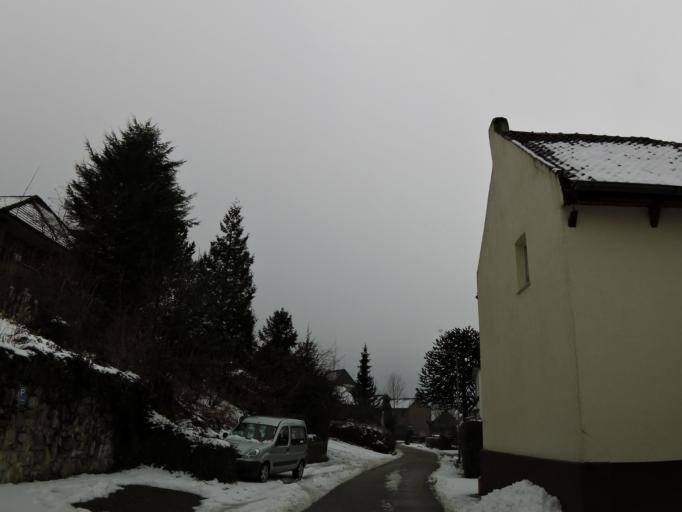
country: NL
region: Limburg
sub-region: Gemeente Vaals
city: Vaals
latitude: 50.7585
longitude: 6.0022
